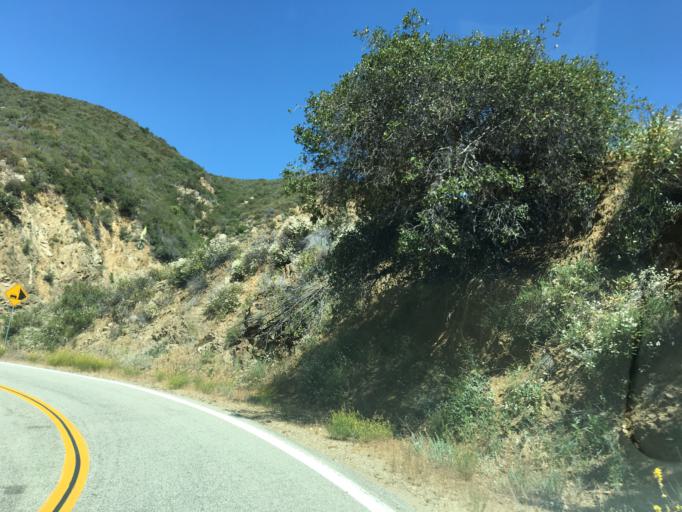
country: US
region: California
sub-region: Los Angeles County
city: Glendora
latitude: 34.2172
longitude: -117.7910
